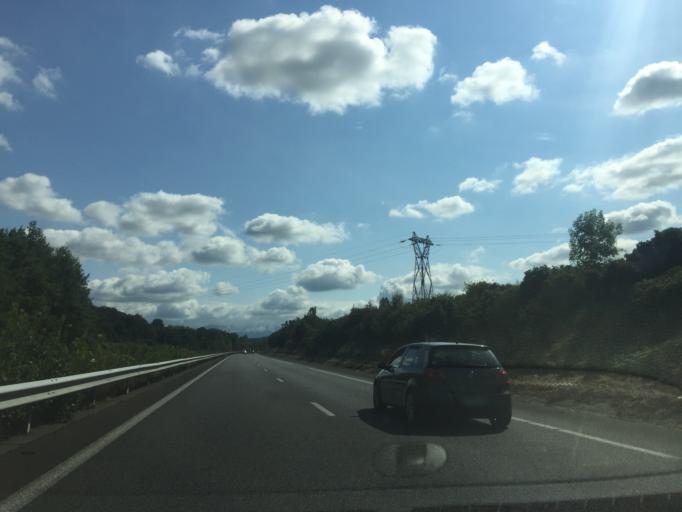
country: FR
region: Midi-Pyrenees
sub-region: Departement de la Haute-Garonne
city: Salies-du-Salat
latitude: 43.1496
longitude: 0.9628
